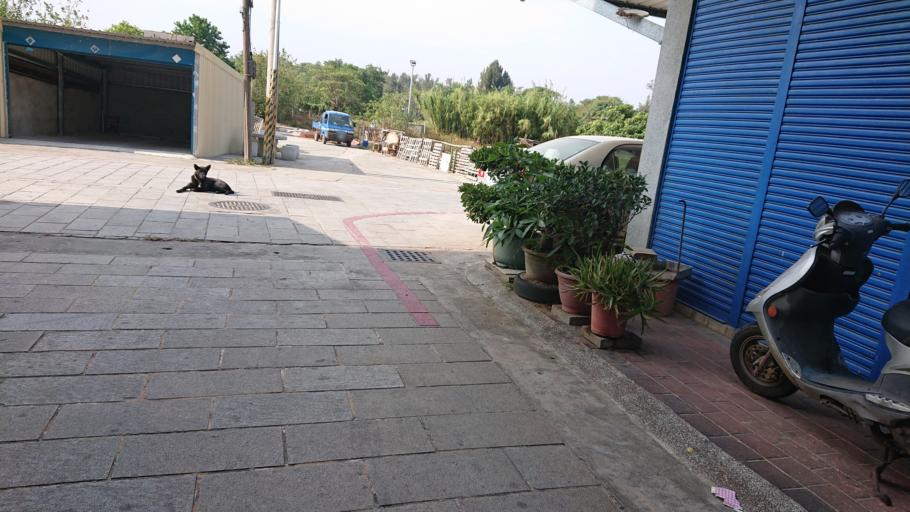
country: TW
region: Fukien
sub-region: Kinmen
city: Jincheng
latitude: 24.4800
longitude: 118.4274
